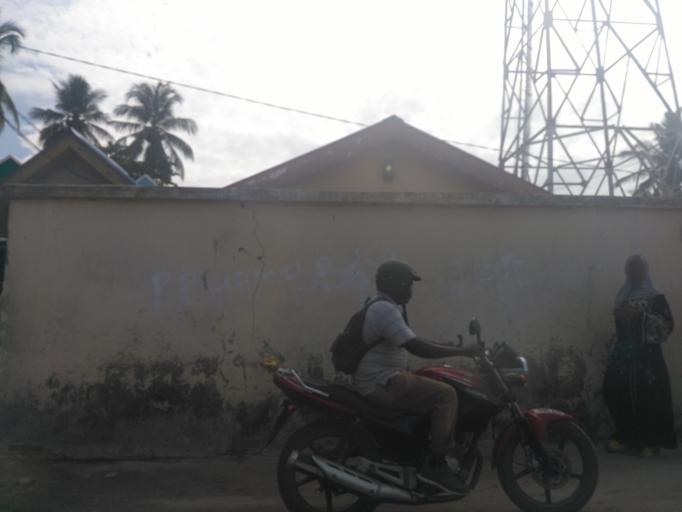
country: TZ
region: Zanzibar Urban/West
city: Zanzibar
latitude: -6.1572
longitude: 39.2075
